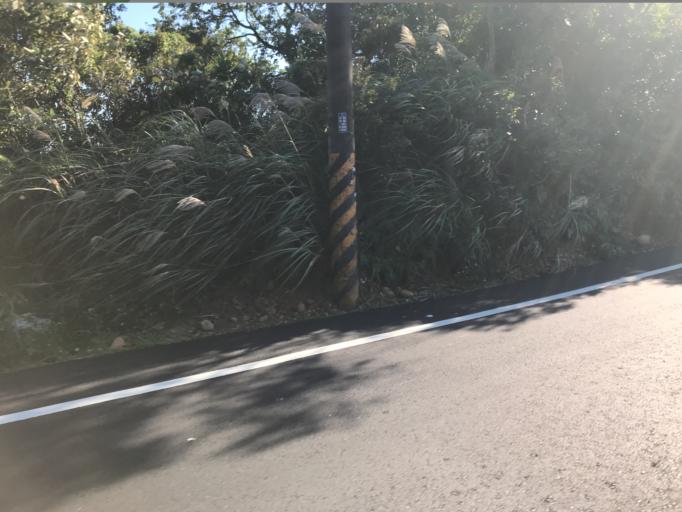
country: TW
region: Taiwan
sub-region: Hsinchu
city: Zhubei
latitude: 24.8688
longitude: 121.0937
